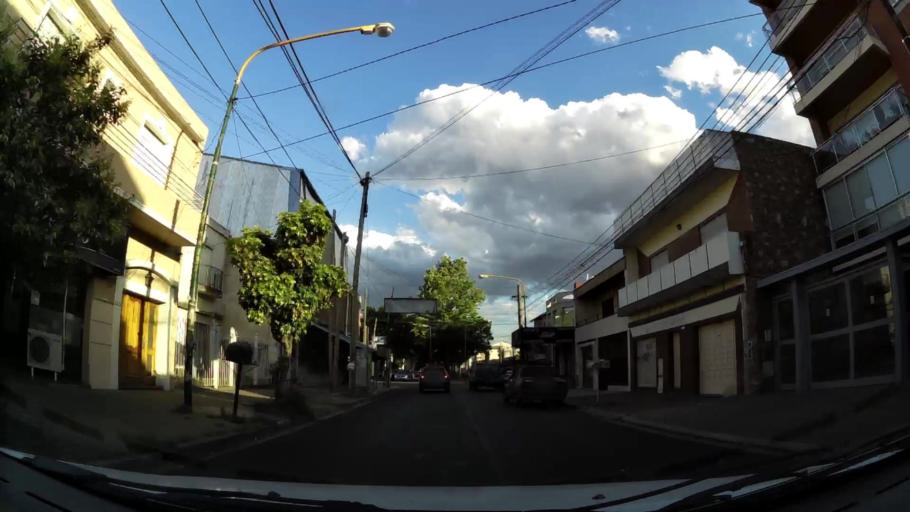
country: AR
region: Buenos Aires
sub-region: Partido de General San Martin
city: General San Martin
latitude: -34.5667
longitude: -58.5436
